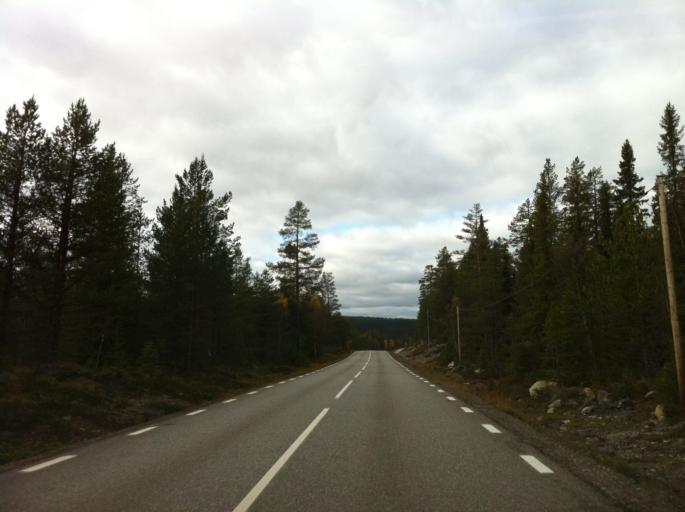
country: NO
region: Hedmark
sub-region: Engerdal
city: Engerdal
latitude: 62.0016
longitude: 12.4308
